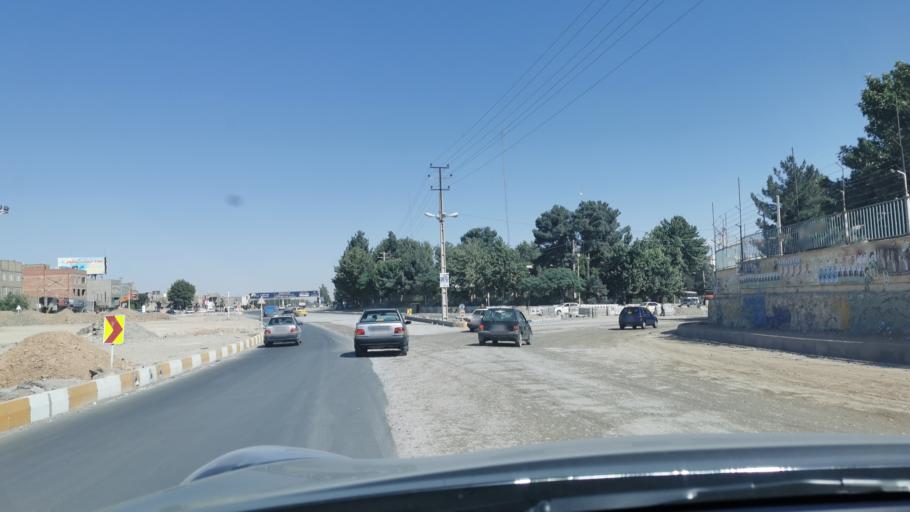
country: IR
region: Razavi Khorasan
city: Chenaran
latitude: 36.6406
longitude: 59.1190
